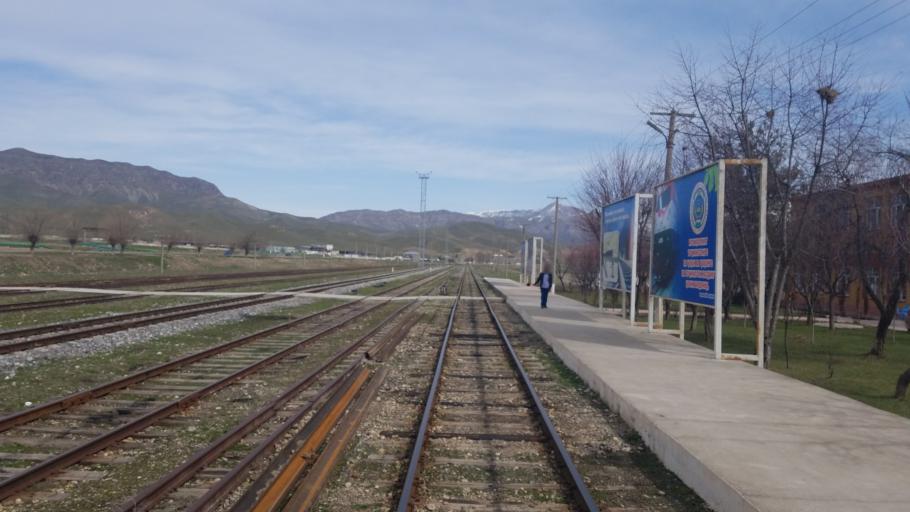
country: TJ
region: Khatlon
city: Yovon
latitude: 38.3048
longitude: 68.9466
